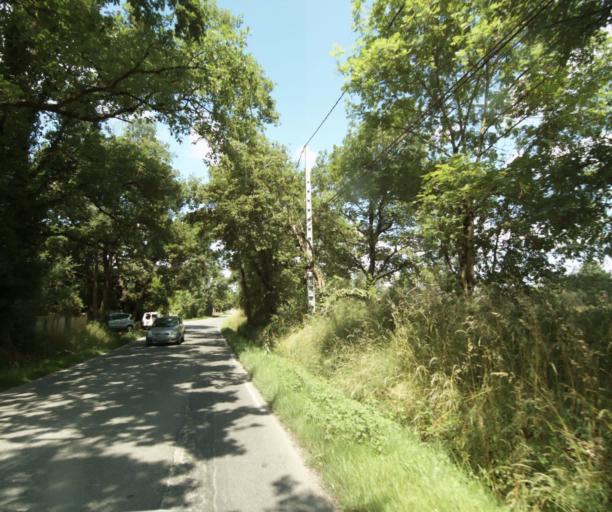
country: FR
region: Midi-Pyrenees
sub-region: Departement du Tarn-et-Garonne
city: Montauban
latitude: 44.0383
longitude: 1.3496
